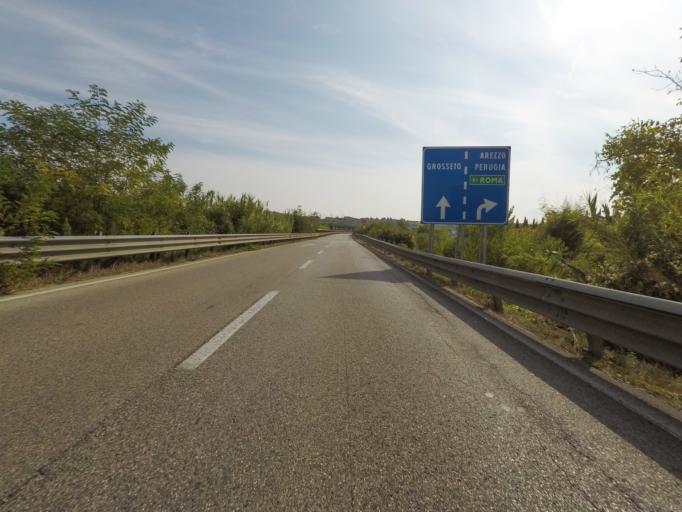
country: IT
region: Tuscany
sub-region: Provincia di Siena
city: Siena
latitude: 43.2960
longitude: 11.3329
